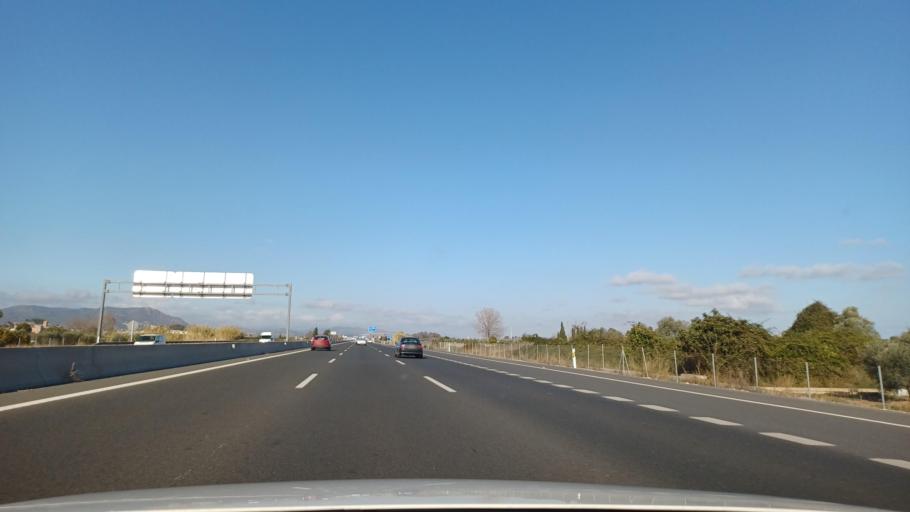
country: ES
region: Valencia
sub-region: Provincia de Valencia
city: Puig
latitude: 39.5711
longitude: -0.2956
